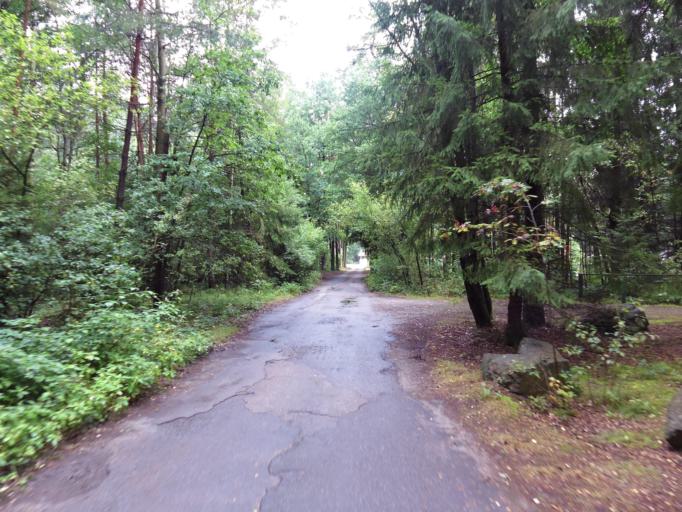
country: CZ
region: Jihocesky
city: Chlum u Trebone
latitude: 48.9831
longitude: 14.9606
